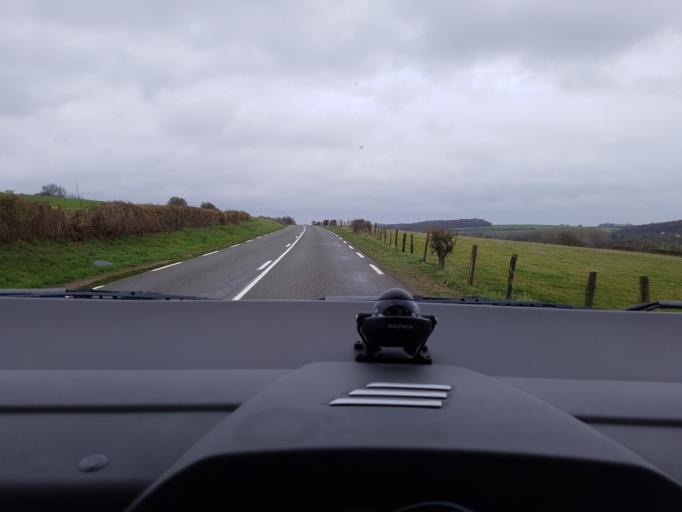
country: FR
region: Picardie
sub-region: Departement de l'Oise
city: Songeons
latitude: 49.5230
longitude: 1.8365
